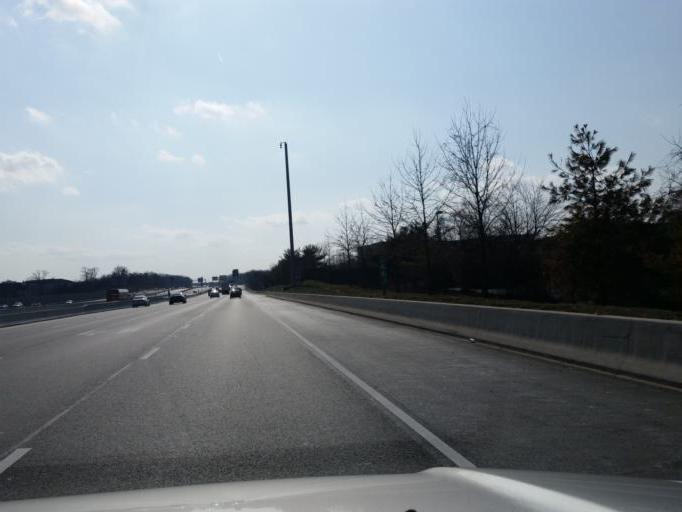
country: US
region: Maryland
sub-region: Baltimore County
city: White Marsh
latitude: 39.3704
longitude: -76.4606
